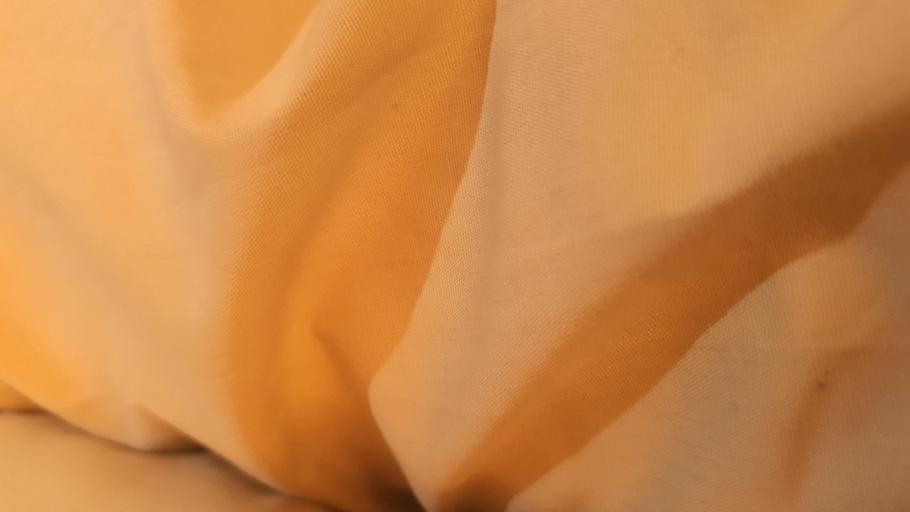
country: PS
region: Gaza Strip
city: Jabalya
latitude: 31.5337
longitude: 34.4609
